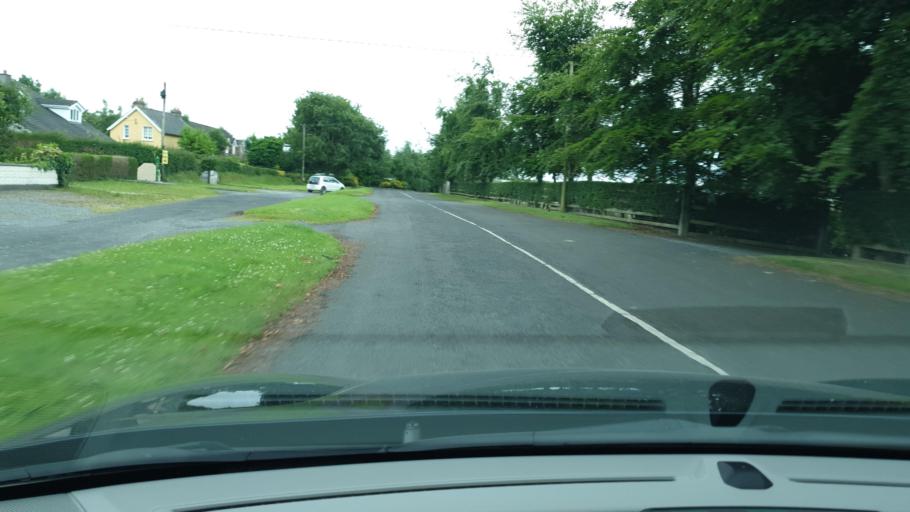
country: IE
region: Leinster
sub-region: An Mhi
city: Dunboyne
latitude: 53.4390
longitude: -6.4722
